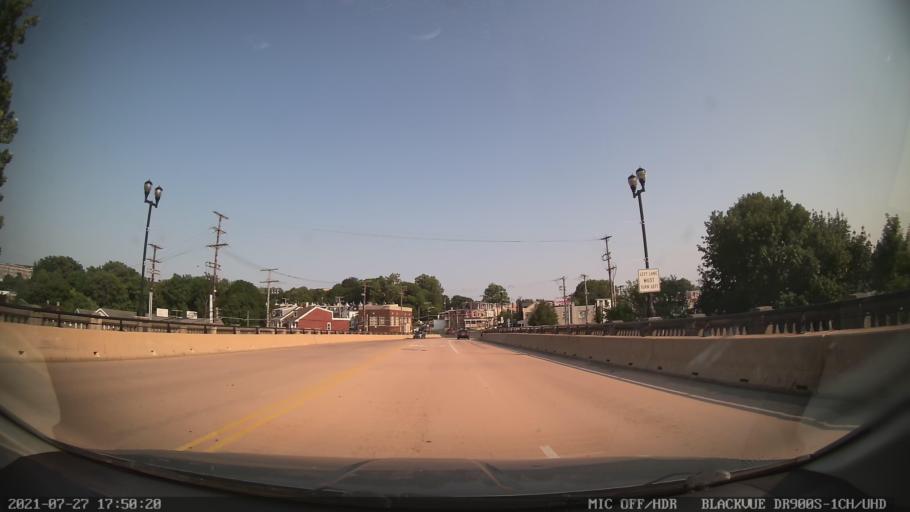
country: US
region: Pennsylvania
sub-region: Berks County
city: West Reading
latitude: 40.3503
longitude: -75.9433
